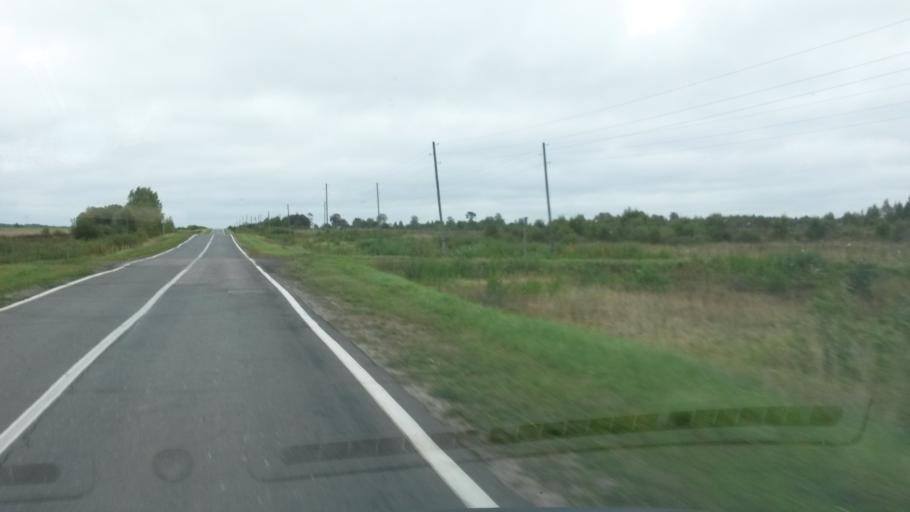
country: RU
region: Jaroslavl
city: Tutayev
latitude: 57.9509
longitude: 39.4315
